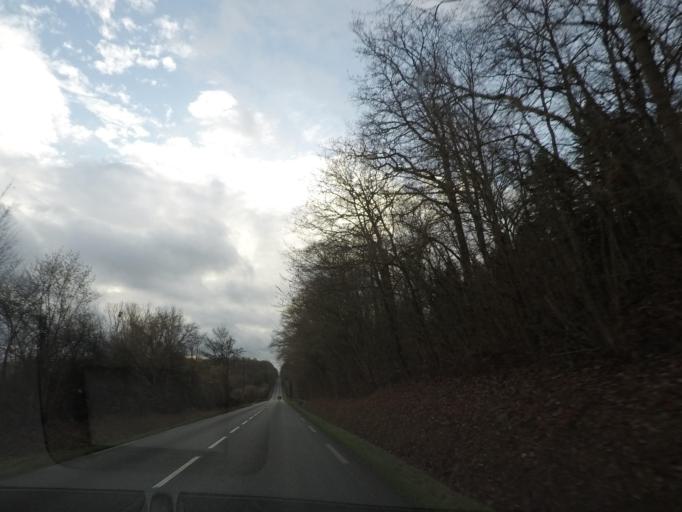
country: FR
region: Pays de la Loire
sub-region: Departement de la Sarthe
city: Cherre
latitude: 48.1431
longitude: 0.6899
